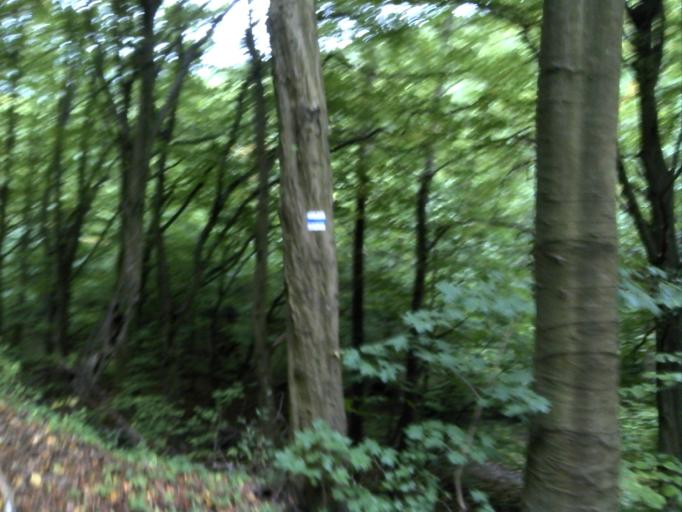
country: HU
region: Borsod-Abauj-Zemplen
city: Satoraljaujhely
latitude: 48.4004
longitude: 21.6014
